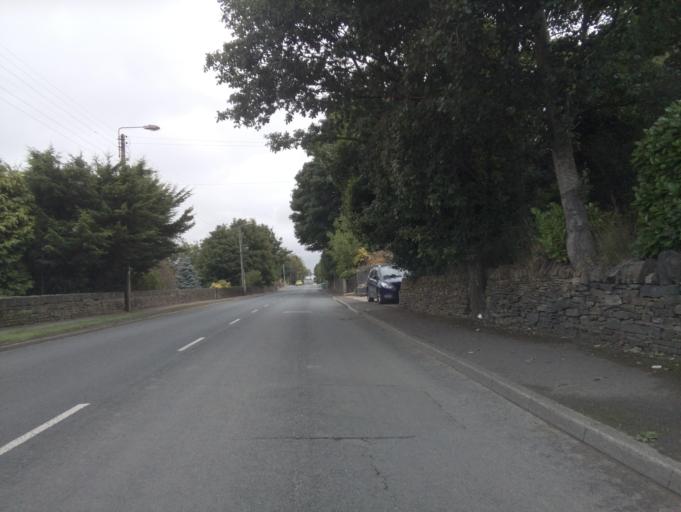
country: GB
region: England
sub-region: Kirklees
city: Holmfirth
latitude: 53.5772
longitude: -1.7789
